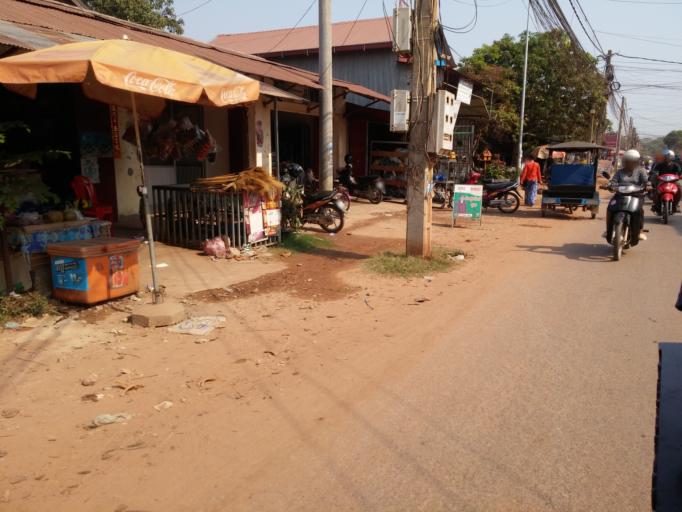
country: KH
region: Siem Reap
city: Siem Reap
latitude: 13.3805
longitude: 103.8519
